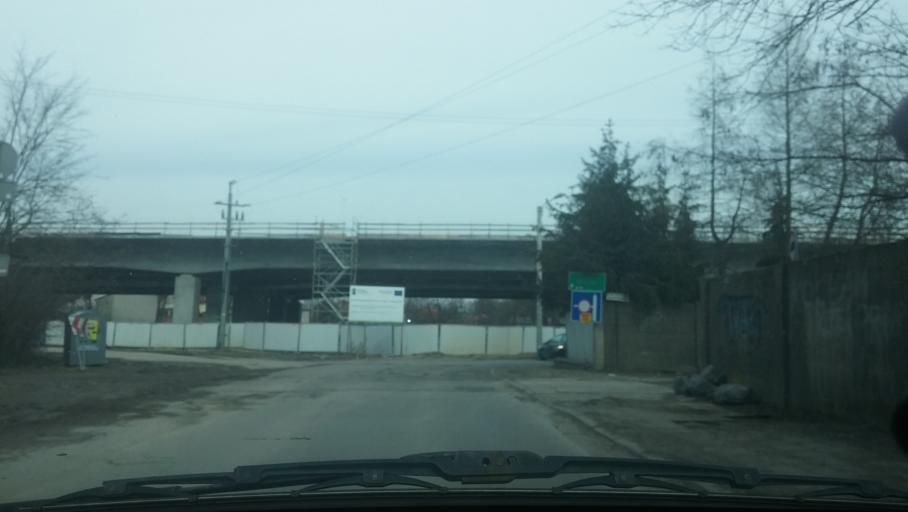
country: PL
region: Masovian Voivodeship
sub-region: Powiat wolominski
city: Marki
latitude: 52.3068
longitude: 21.1051
